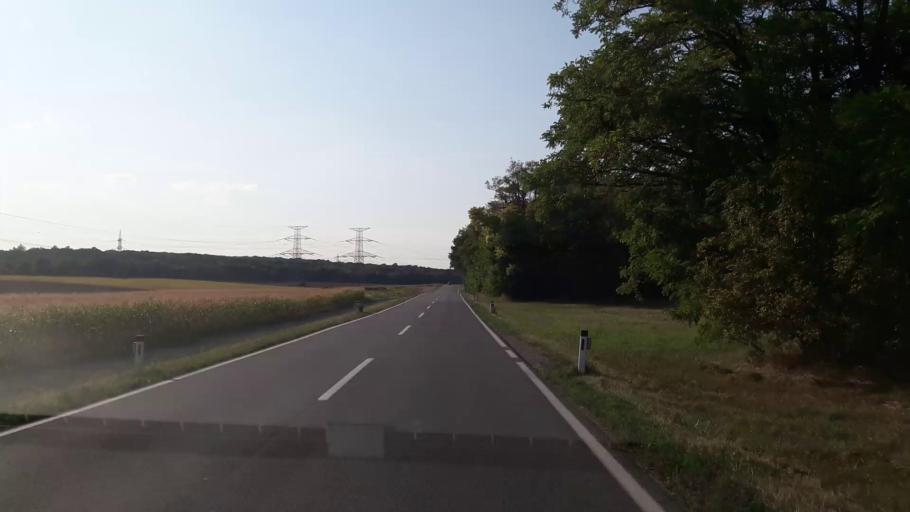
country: AT
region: Lower Austria
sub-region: Politischer Bezirk Ganserndorf
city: Orth an der Donau
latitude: 48.0761
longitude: 16.6873
